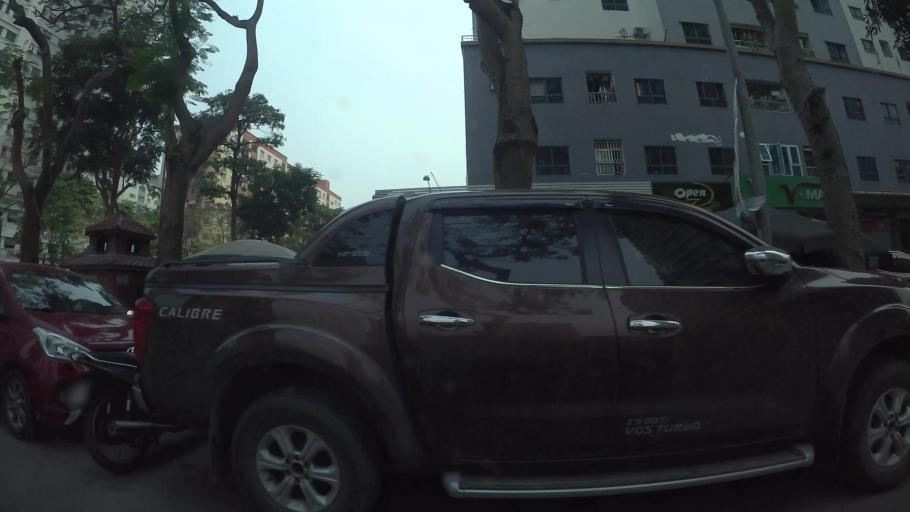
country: VN
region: Ha Noi
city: Van Dien
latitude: 20.9636
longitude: 105.8314
